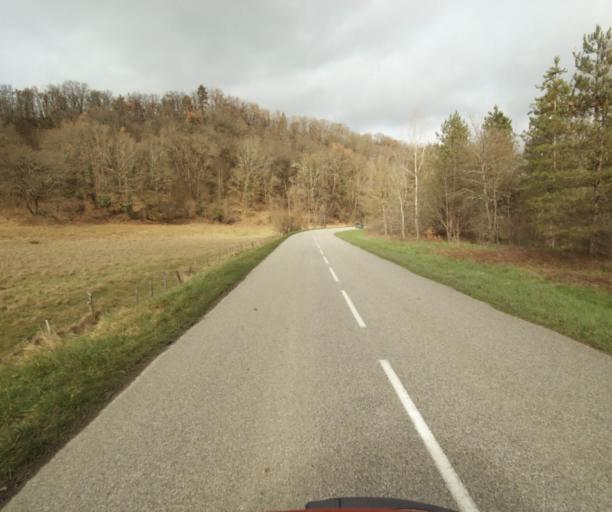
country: FR
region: Midi-Pyrenees
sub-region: Departement de l'Ariege
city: Pamiers
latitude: 43.1454
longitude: 1.5900
